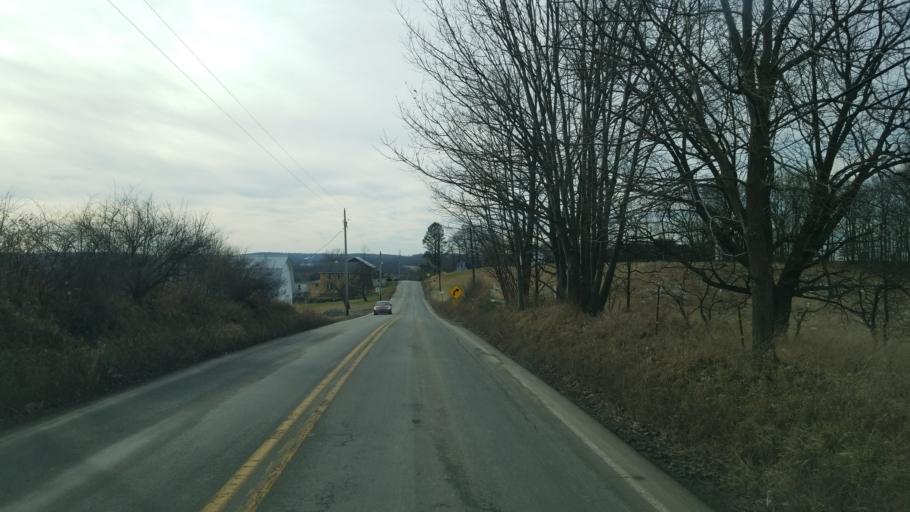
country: US
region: Pennsylvania
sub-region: Jefferson County
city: Punxsutawney
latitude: 40.8798
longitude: -79.0694
